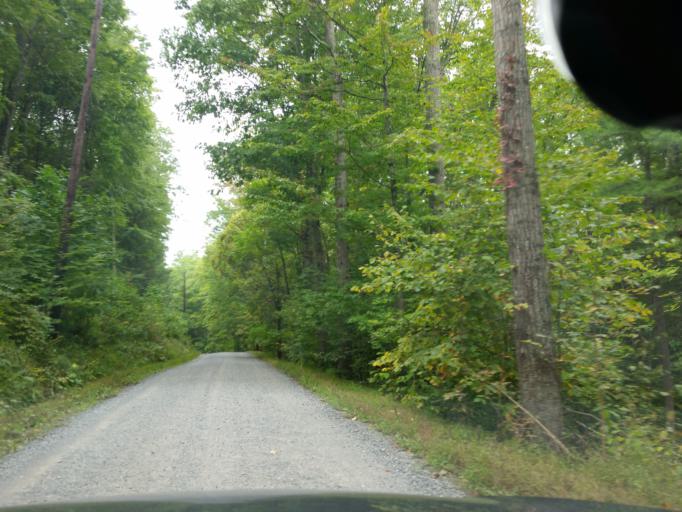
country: US
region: Pennsylvania
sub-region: Union County
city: Mifflinburg
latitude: 40.9862
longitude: -77.0738
